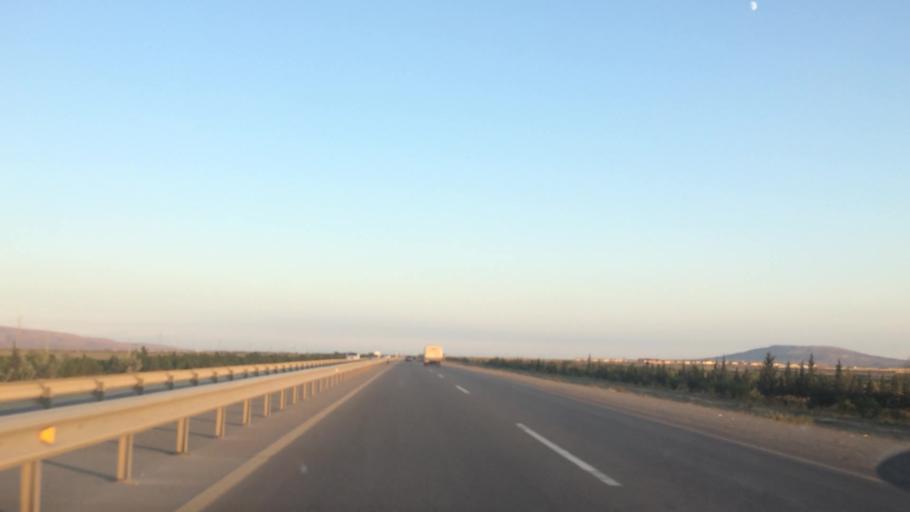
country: AZ
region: Baki
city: Qobustan
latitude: 39.9903
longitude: 49.1984
